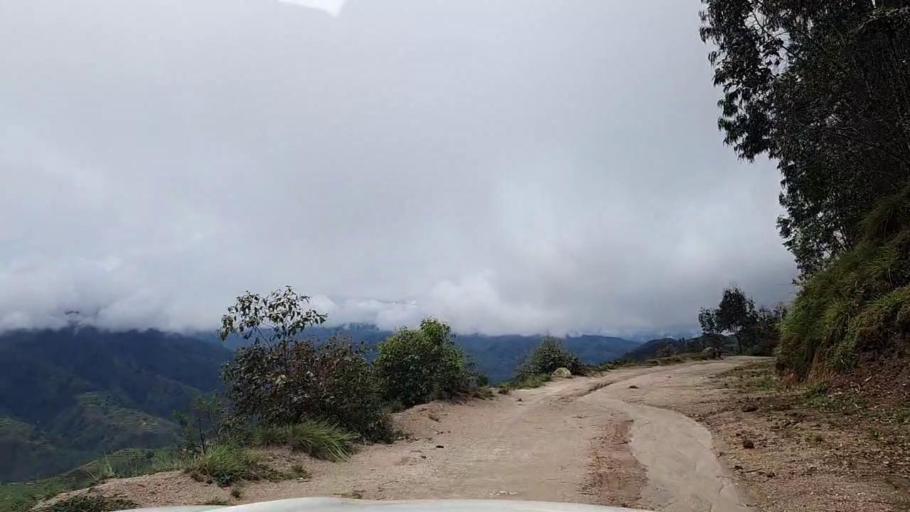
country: RW
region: Southern Province
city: Gikongoro
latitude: -2.3689
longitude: 29.4965
